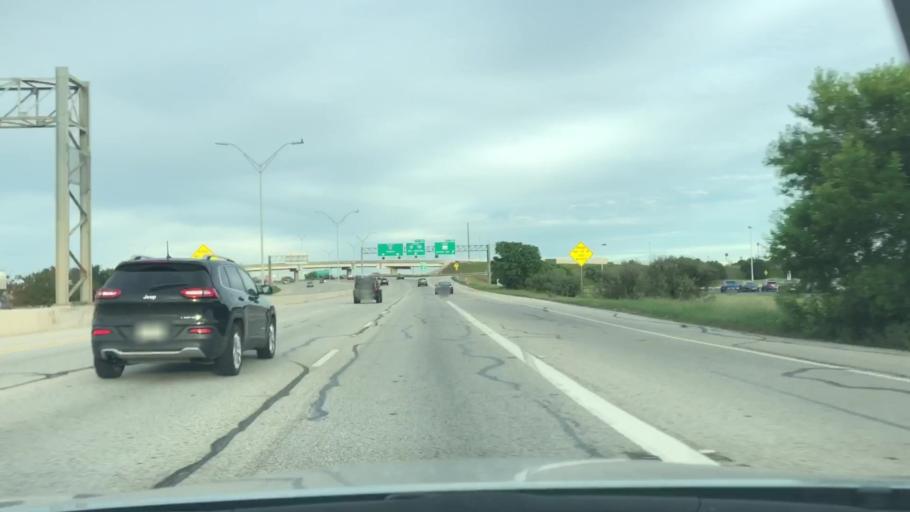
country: US
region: Texas
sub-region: Bexar County
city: Windcrest
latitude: 29.5159
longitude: -98.4066
